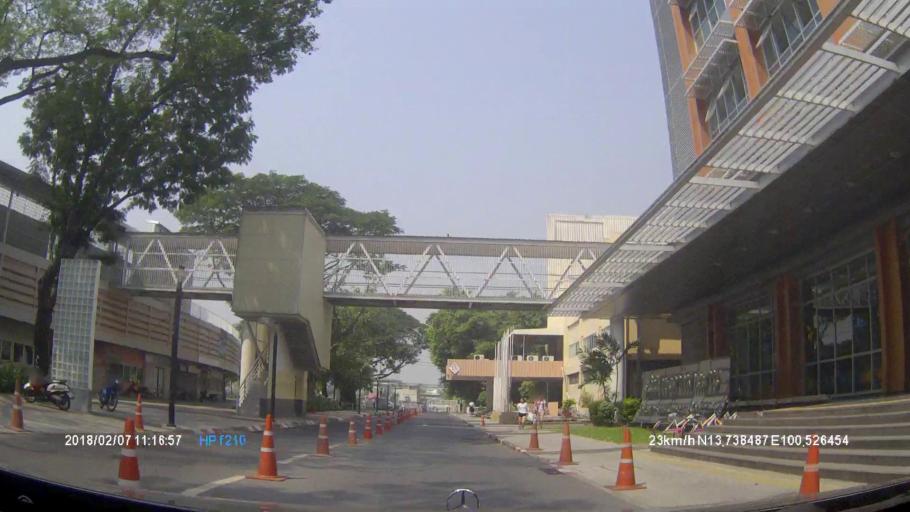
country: TH
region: Bangkok
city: Pathum Wan
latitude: 13.7385
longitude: 100.5264
